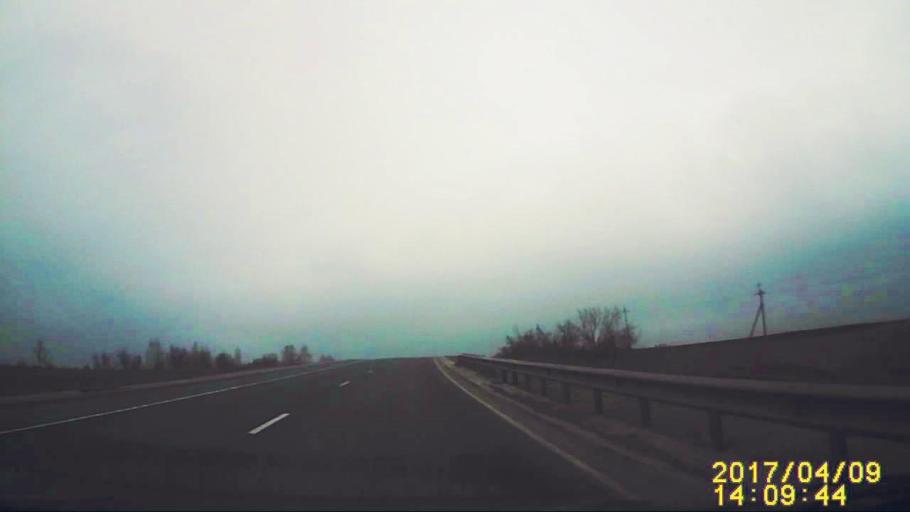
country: RU
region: Ulyanovsk
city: Krasnyy Gulyay
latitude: 54.0314
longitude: 48.2128
